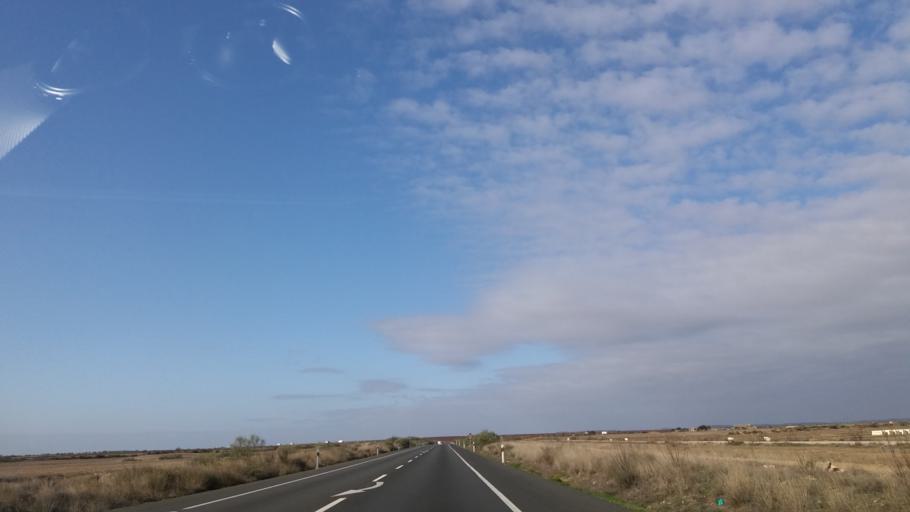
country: ES
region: Aragon
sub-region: Provincia de Huesca
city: Candasnos
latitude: 41.5187
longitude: 0.1360
